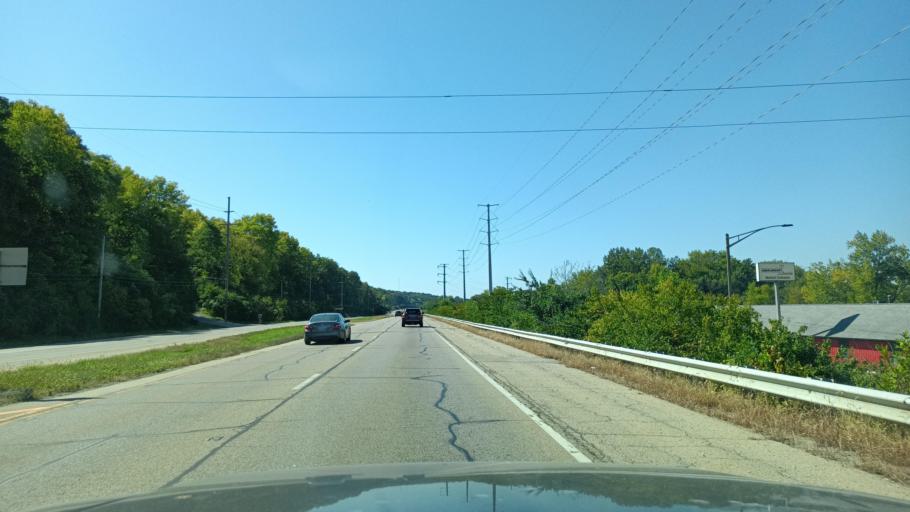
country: US
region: Illinois
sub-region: Tazewell County
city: East Peoria
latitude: 40.6896
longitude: -89.5459
